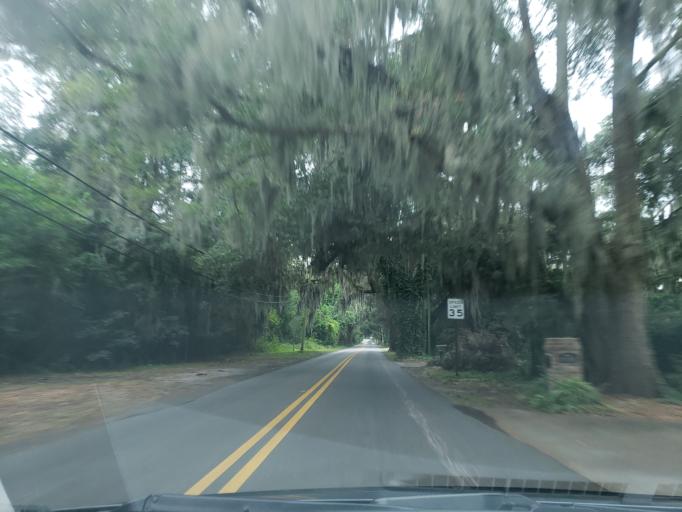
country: US
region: Georgia
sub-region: Chatham County
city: Montgomery
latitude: 31.9614
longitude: -81.1018
